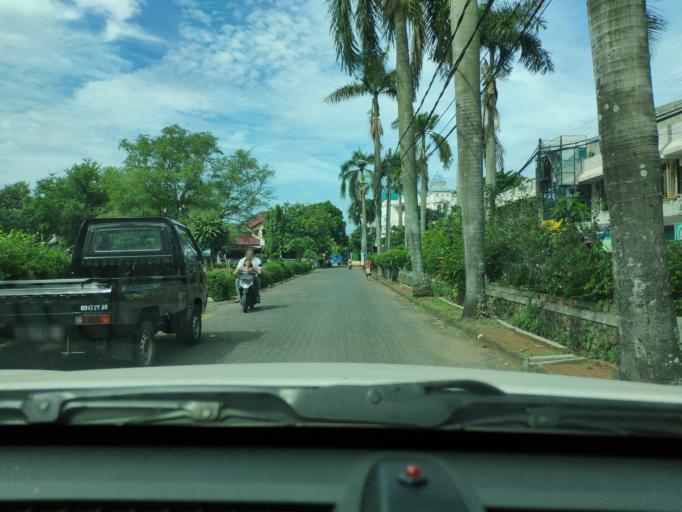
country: ID
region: West Java
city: Ciputat
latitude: -6.2242
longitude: 106.7108
